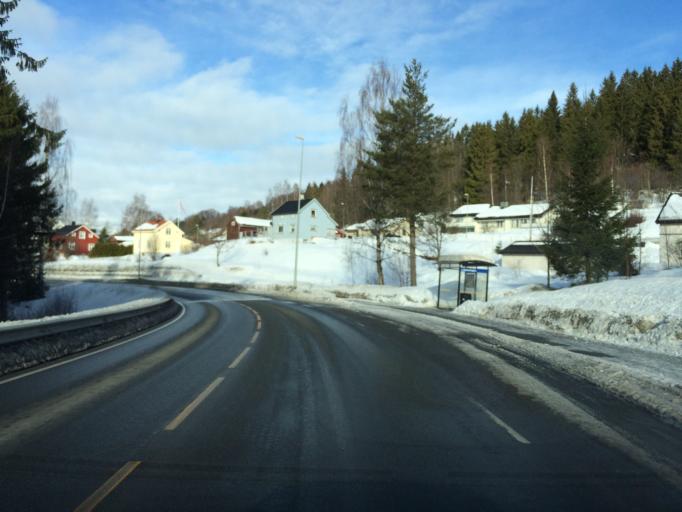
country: NO
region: Oppland
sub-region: Gausdal
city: Segalstad bru
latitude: 61.2246
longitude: 10.2321
